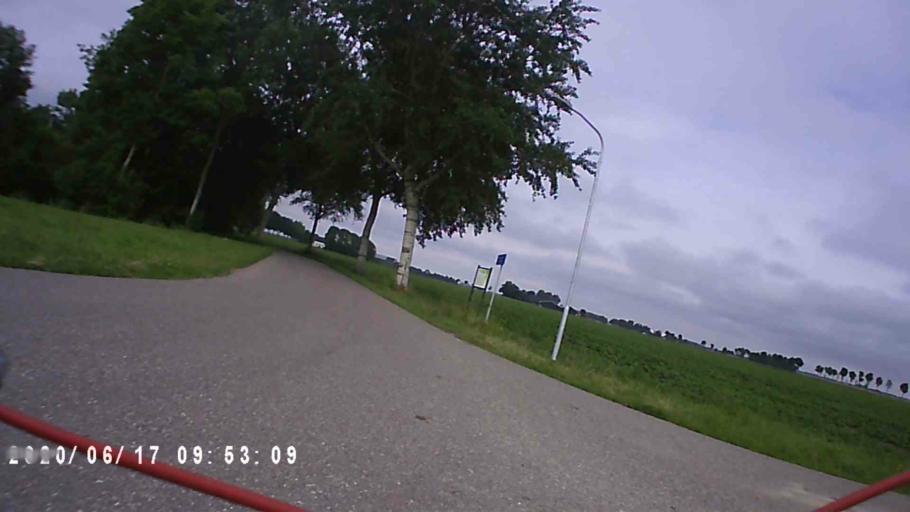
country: NL
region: Groningen
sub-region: Gemeente De Marne
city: Ulrum
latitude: 53.3606
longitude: 6.3196
